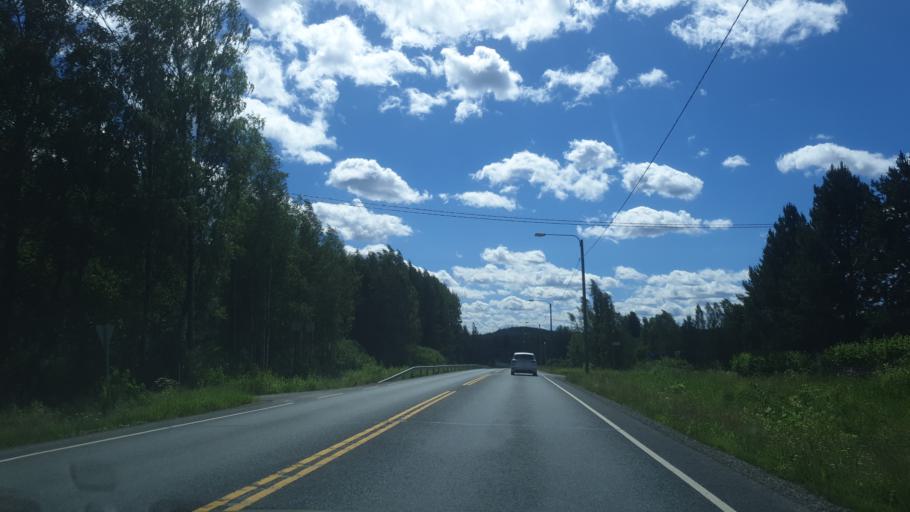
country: FI
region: Northern Savo
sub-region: Varkaus
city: Leppaevirta
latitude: 62.6431
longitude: 27.6081
